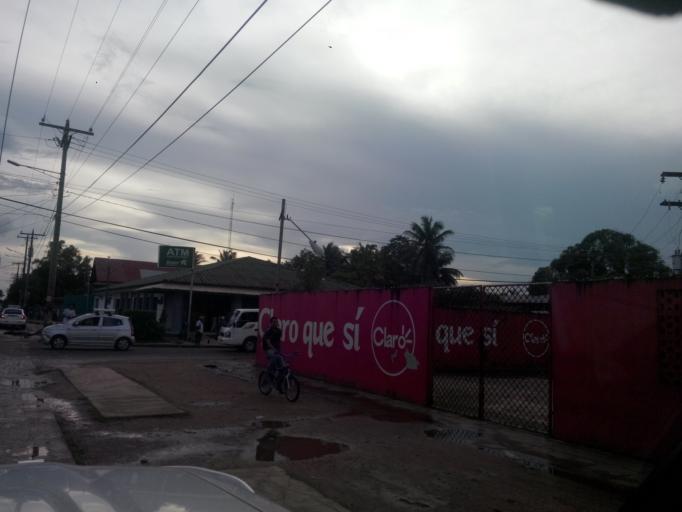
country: NI
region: Atlantico Norte (RAAN)
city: Puerto Cabezas
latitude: 14.0277
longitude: -83.3820
